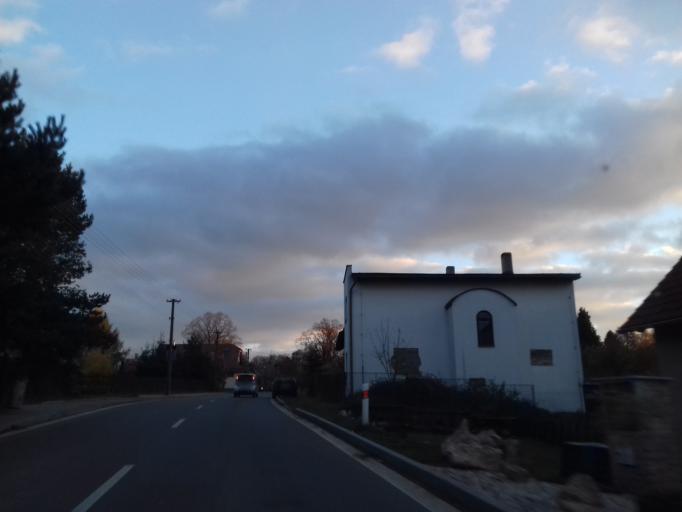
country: CZ
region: Pardubicky
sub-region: Okres Chrudim
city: Hlinsko
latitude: 49.7912
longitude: 15.9250
